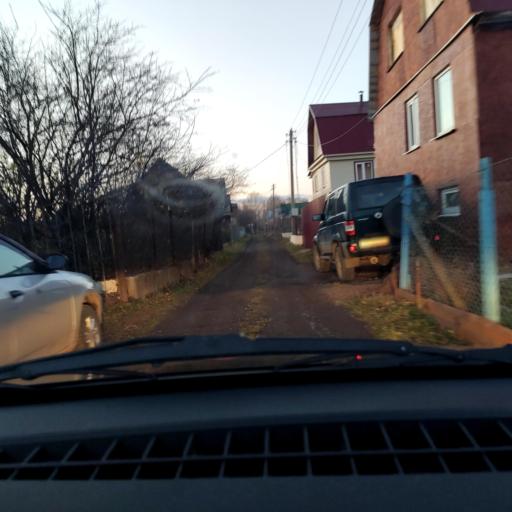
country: RU
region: Bashkortostan
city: Ufa
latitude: 54.6486
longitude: 55.8990
